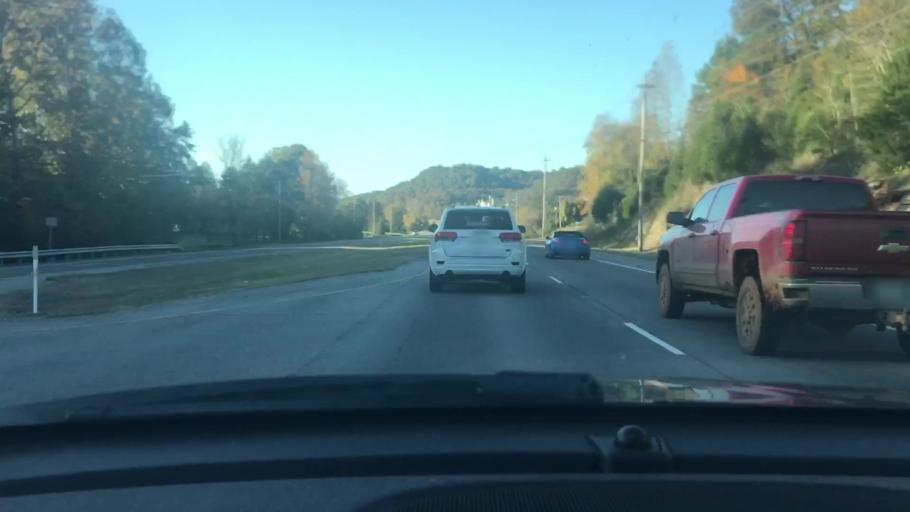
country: US
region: Tennessee
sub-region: Cheatham County
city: Ashland City
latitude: 36.2378
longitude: -87.0209
